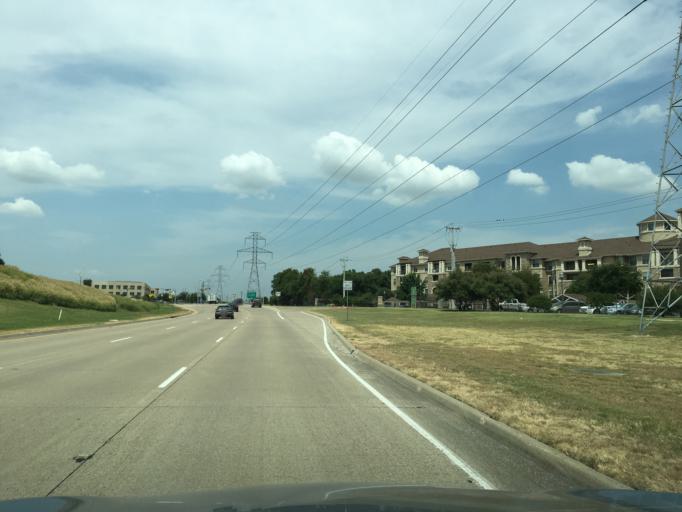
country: US
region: Texas
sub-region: Collin County
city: Plano
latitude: 33.0044
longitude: -96.7461
